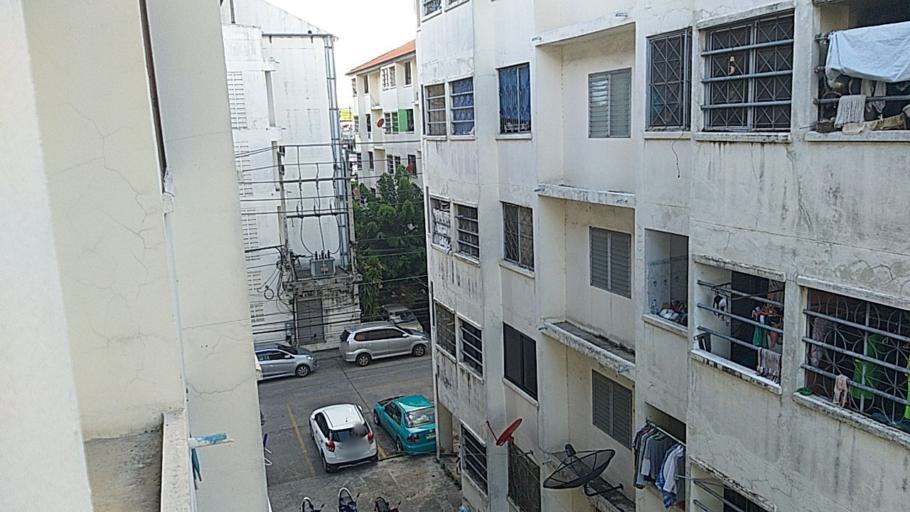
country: TH
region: Bangkok
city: Sai Mai
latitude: 13.9319
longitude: 100.6871
